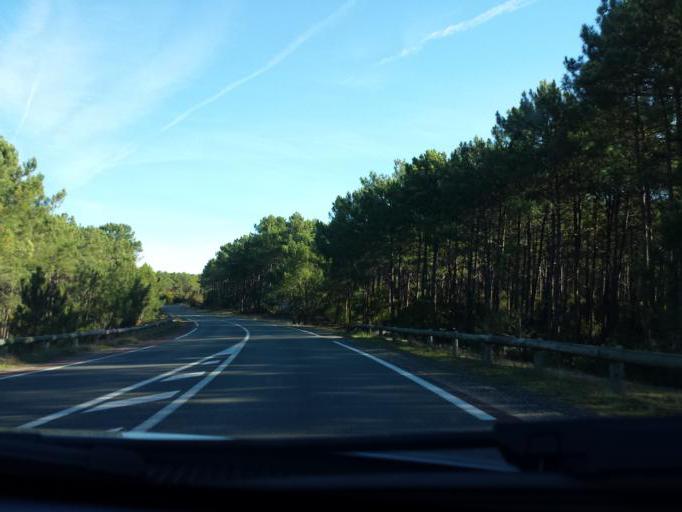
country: FR
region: Aquitaine
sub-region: Departement de la Gironde
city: Lacanau
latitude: 45.0037
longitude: -1.1506
